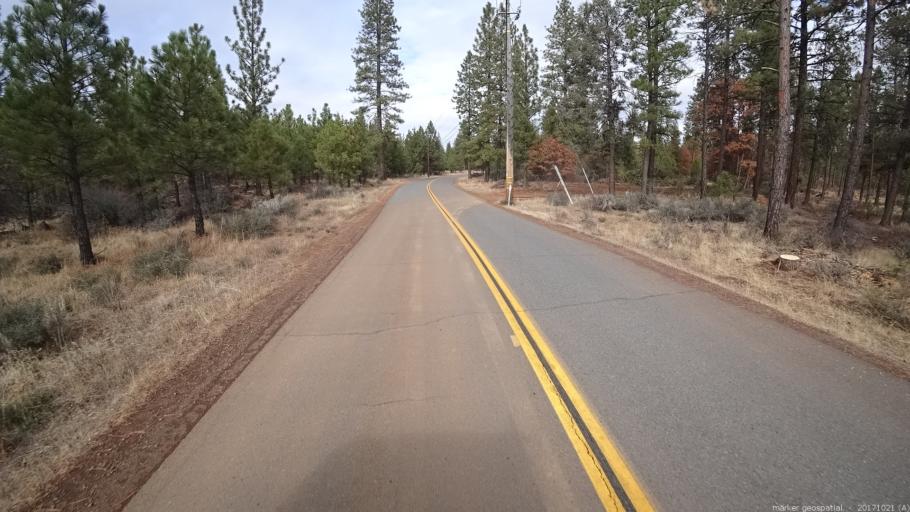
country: US
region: California
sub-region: Shasta County
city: Burney
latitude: 40.9270
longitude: -121.6454
